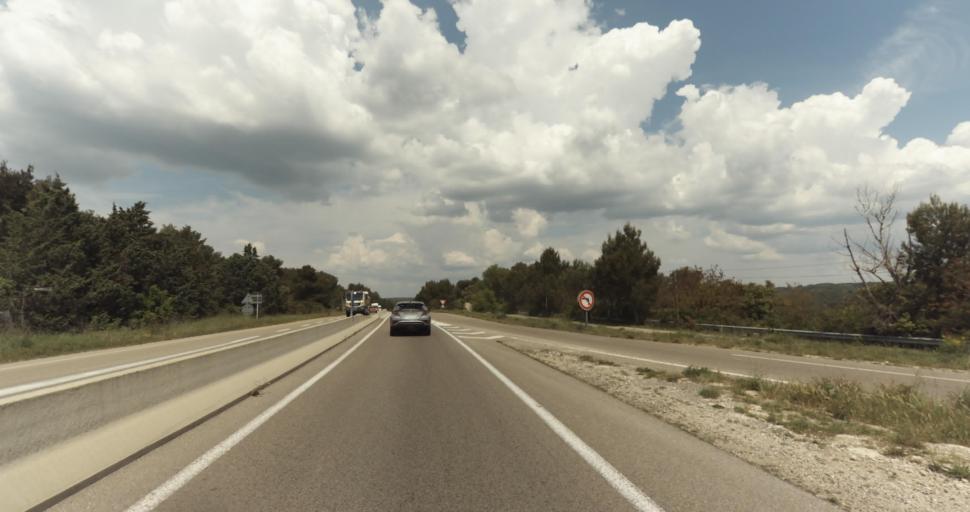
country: FR
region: Languedoc-Roussillon
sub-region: Departement du Gard
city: Nimes
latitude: 43.8589
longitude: 4.3242
